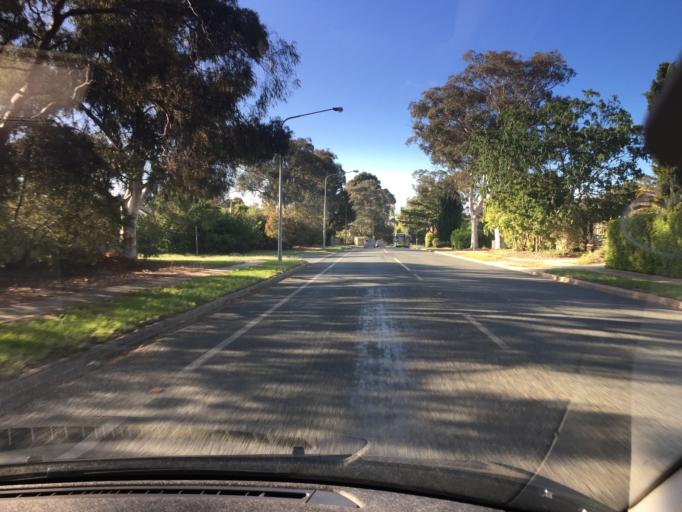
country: AU
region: Australian Capital Territory
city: Kaleen
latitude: -35.2278
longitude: 149.1113
